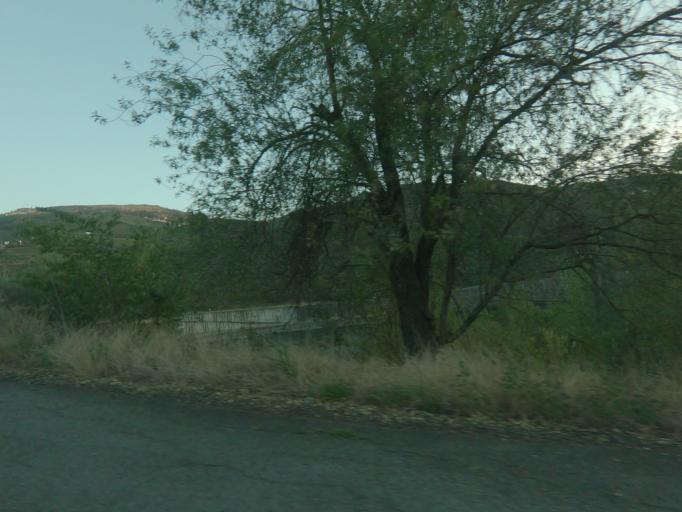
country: PT
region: Vila Real
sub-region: Peso da Regua
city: Peso da Regua
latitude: 41.1488
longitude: -7.7412
